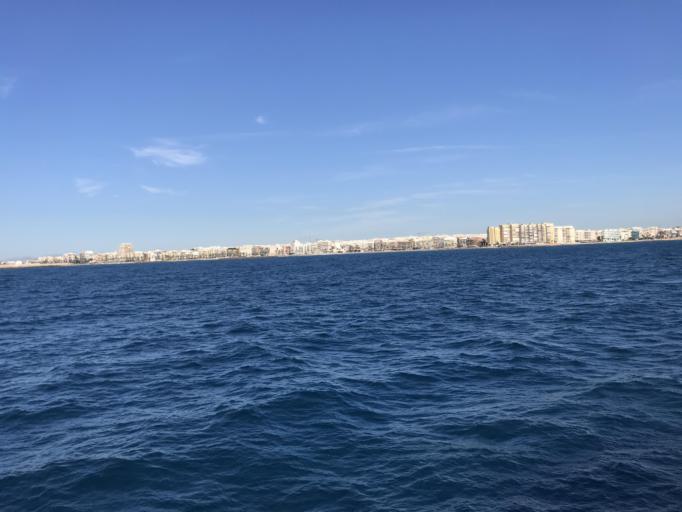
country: ES
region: Valencia
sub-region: Provincia de Alicante
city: Torrevieja
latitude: 37.9675
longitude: -0.6628
